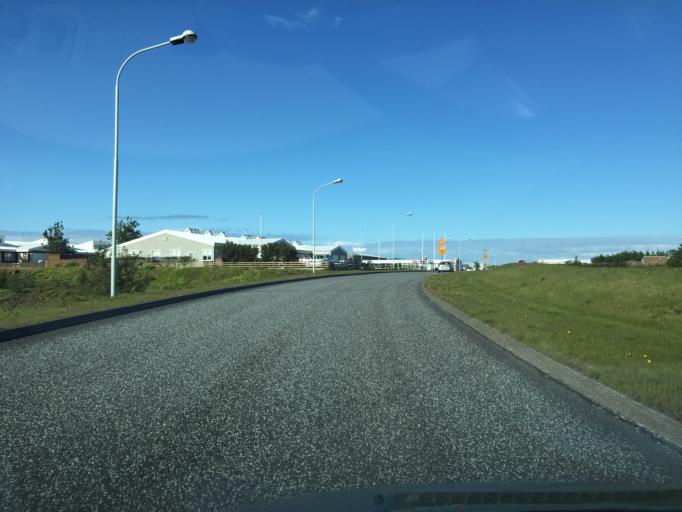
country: IS
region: Southern Peninsula
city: Reykjanesbaer
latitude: 64.0008
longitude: -22.5735
